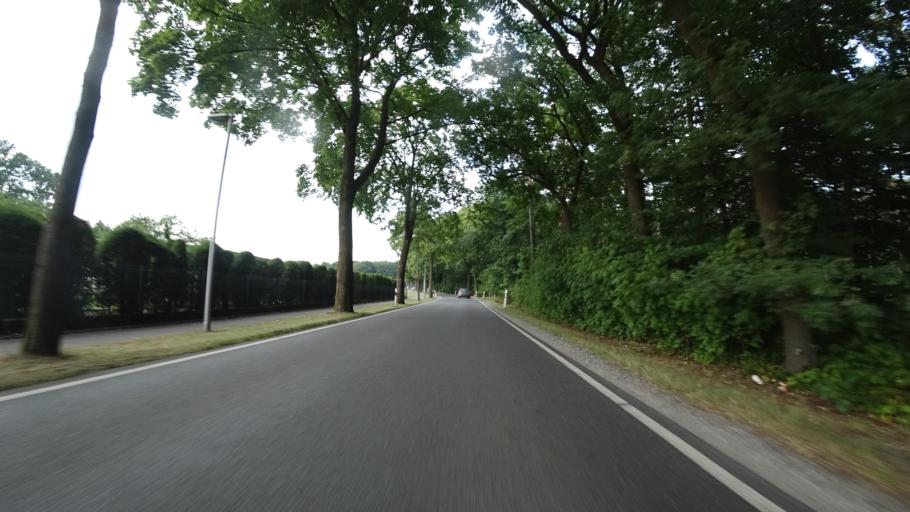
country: DE
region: North Rhine-Westphalia
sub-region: Regierungsbezirk Detmold
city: Steinhagen
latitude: 51.9853
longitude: 8.4636
